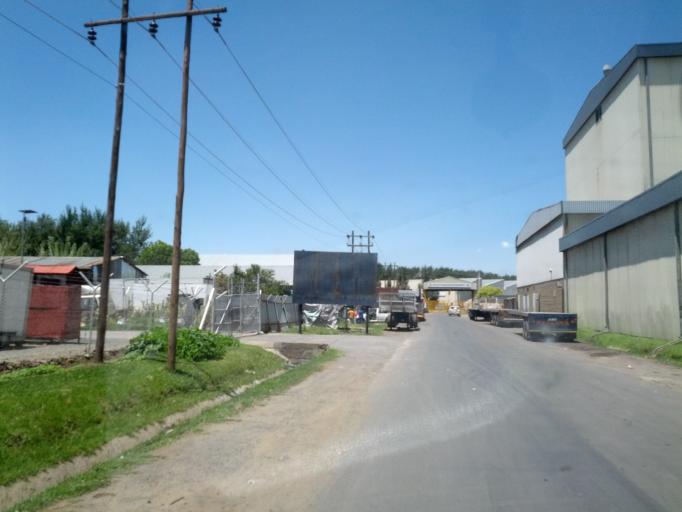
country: LS
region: Maseru
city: Maseru
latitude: -29.2952
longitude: 27.4815
